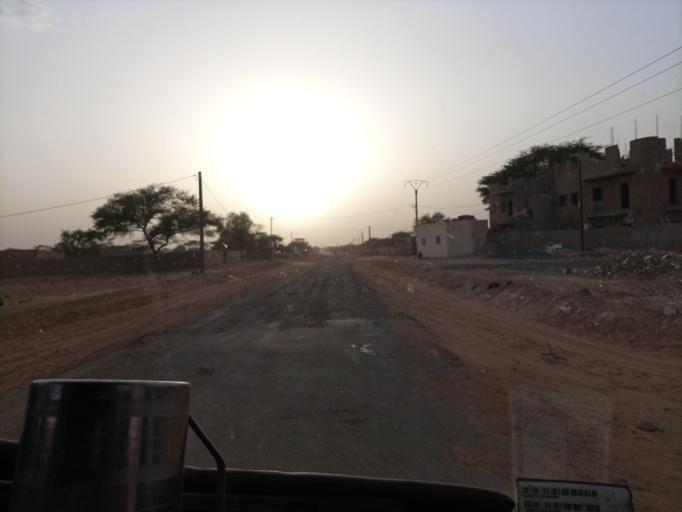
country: SN
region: Louga
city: Dara
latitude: 15.4006
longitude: -15.6551
